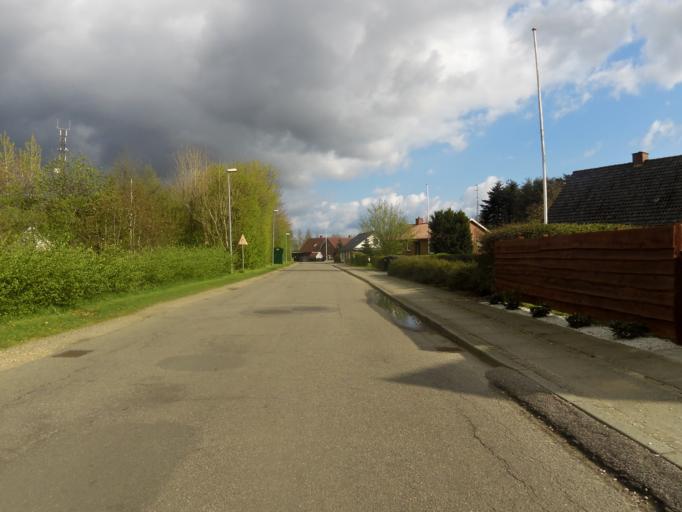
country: DK
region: South Denmark
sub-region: Haderslev Kommune
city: Gram
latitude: 55.2522
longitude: 8.9606
